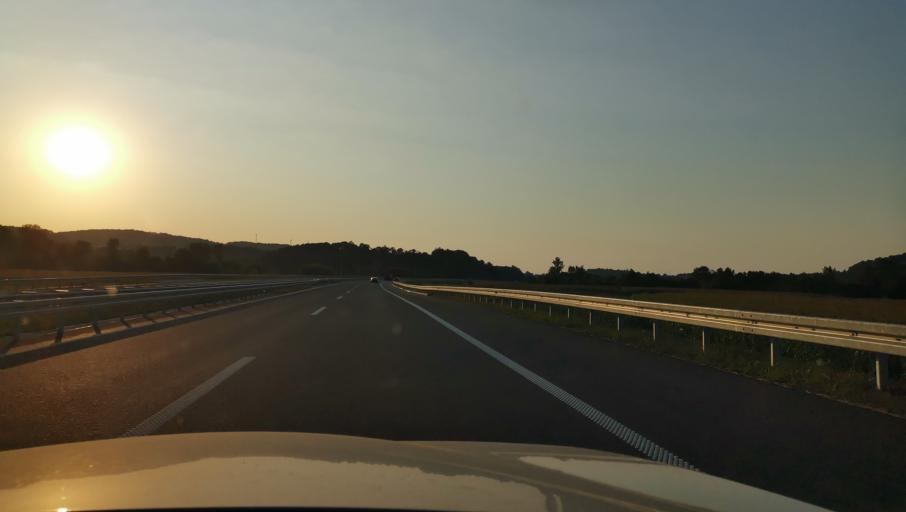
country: RS
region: Central Serbia
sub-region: Kolubarski Okrug
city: Lajkovac
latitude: 44.3343
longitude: 20.2053
